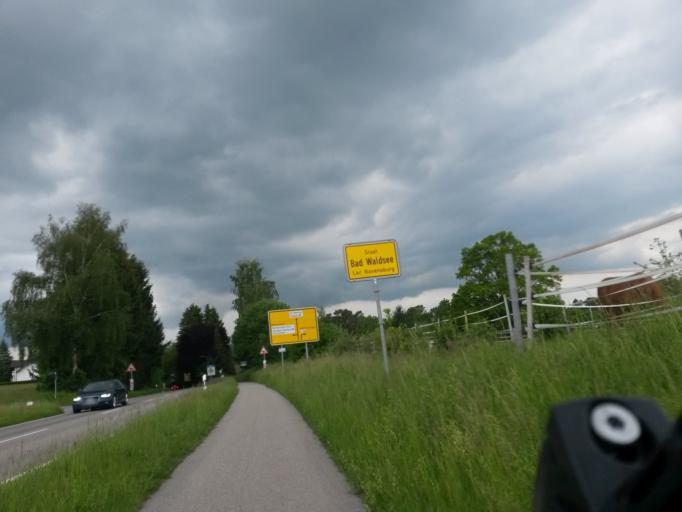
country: DE
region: Baden-Wuerttemberg
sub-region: Tuebingen Region
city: Bad Waldsee
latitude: 47.9234
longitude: 9.7683
